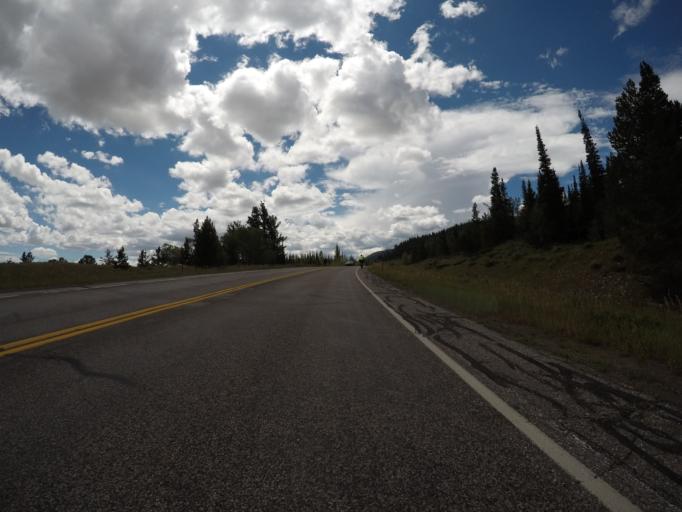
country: US
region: Wyoming
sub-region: Albany County
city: Laramie
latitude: 41.3224
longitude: -106.1566
